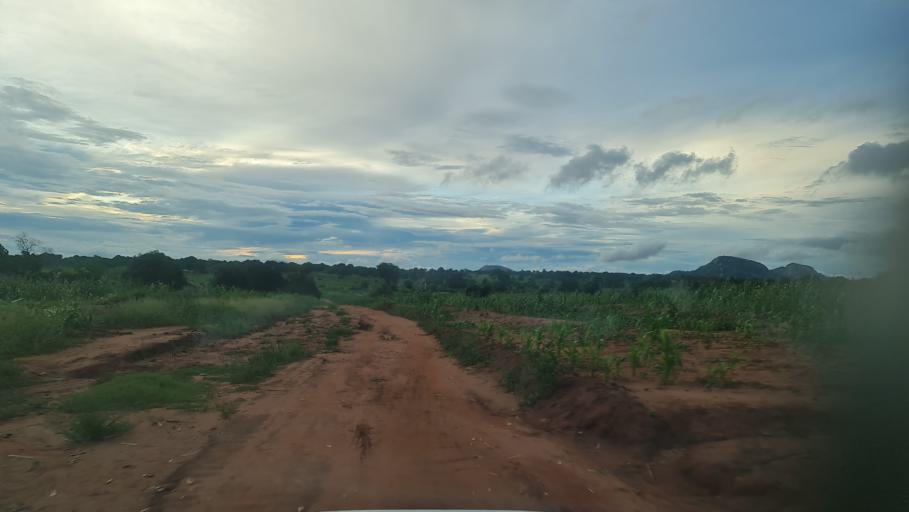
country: MZ
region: Nampula
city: Nacala
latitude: -14.7429
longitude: 39.9508
